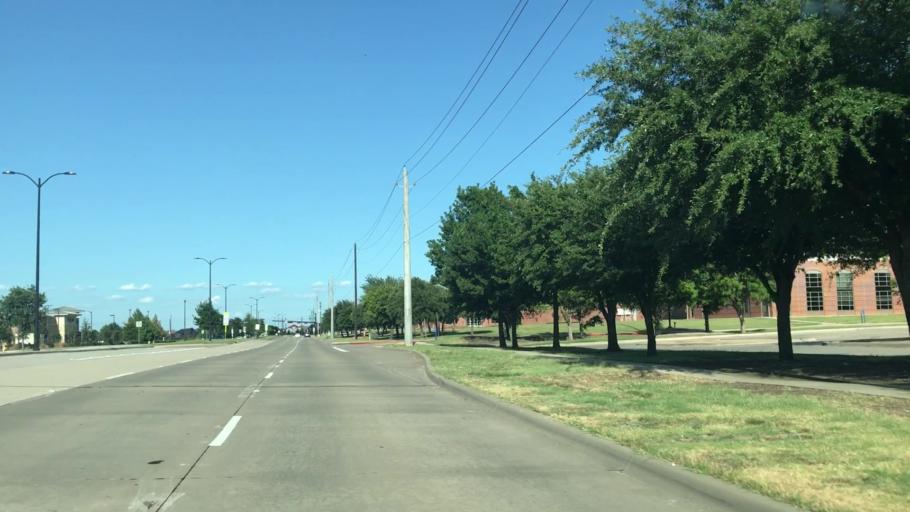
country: US
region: Texas
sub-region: Collin County
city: Frisco
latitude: 33.1374
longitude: -96.7715
